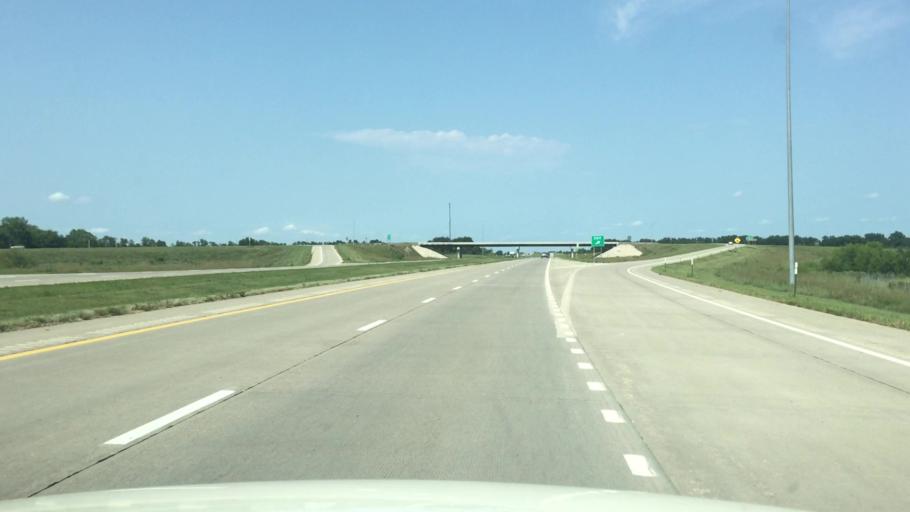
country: US
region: Kansas
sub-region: Linn County
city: Pleasanton
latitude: 38.1427
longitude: -94.7098
